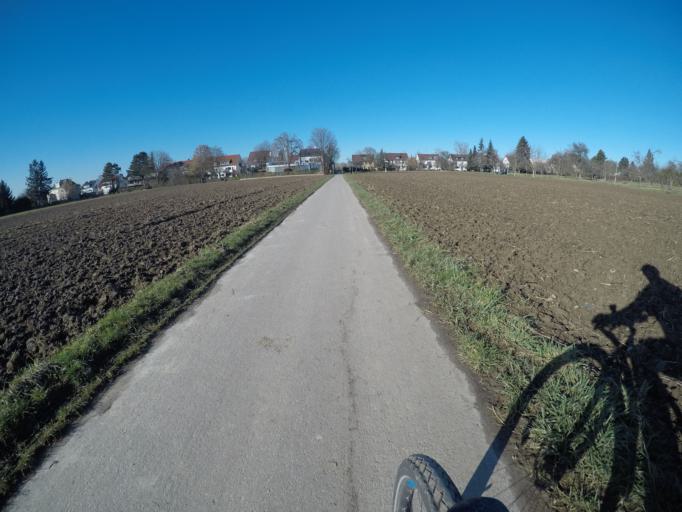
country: DE
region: Baden-Wuerttemberg
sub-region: Regierungsbezirk Stuttgart
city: Leinfelden-Echterdingen
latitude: 48.7375
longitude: 9.1470
